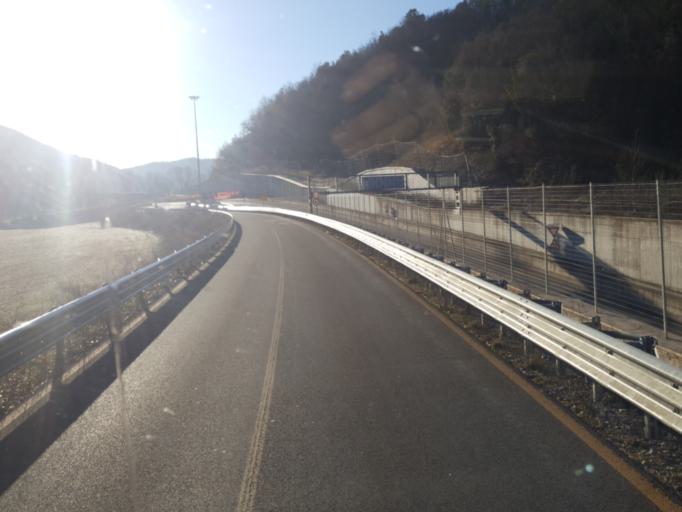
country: IT
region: Latium
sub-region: Provincia di Rieti
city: Colli sul Velino
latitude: 42.5276
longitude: 12.7307
